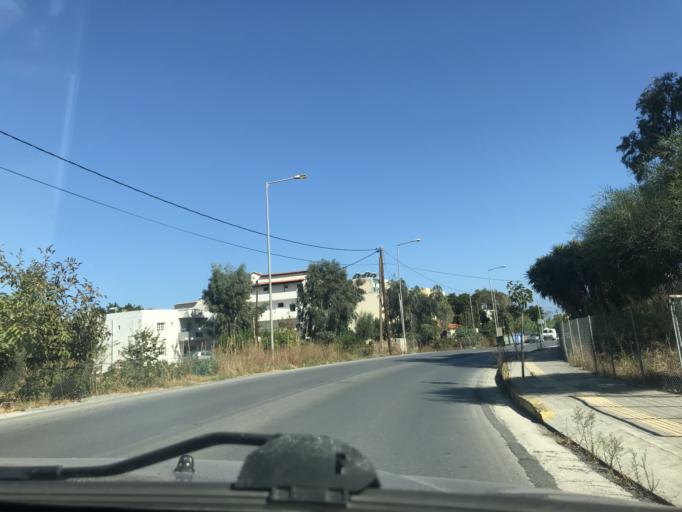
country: GR
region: Crete
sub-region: Nomos Irakleiou
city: Gazi
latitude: 35.3332
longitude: 25.0643
